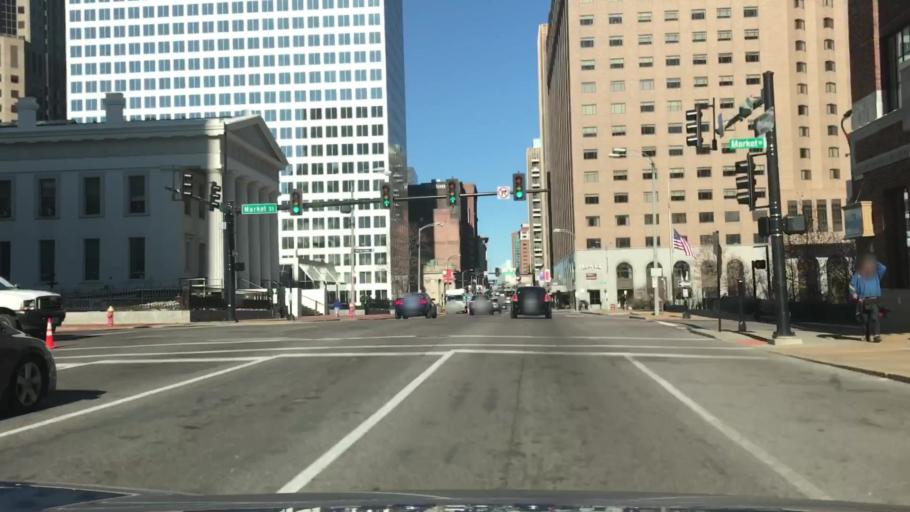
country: US
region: Missouri
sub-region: City of Saint Louis
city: St. Louis
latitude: 38.6249
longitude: -90.1889
